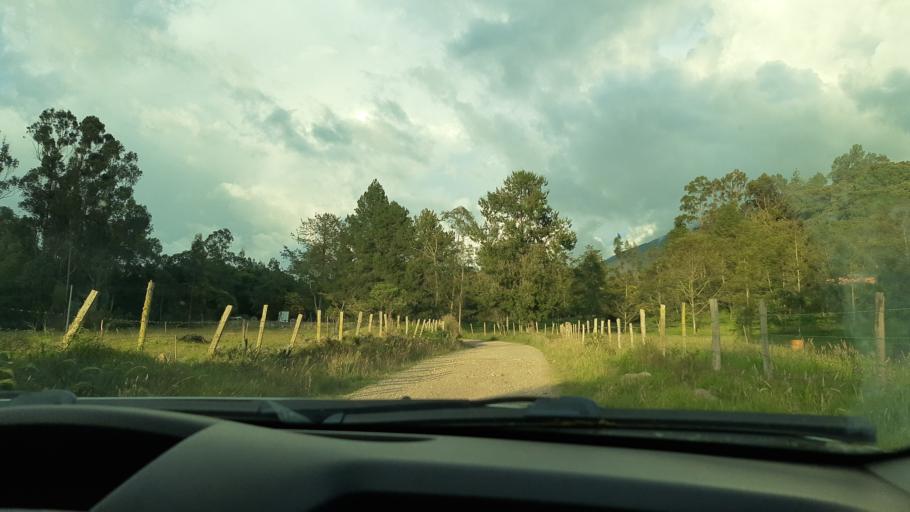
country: CO
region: Boyaca
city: La Capilla
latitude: 5.7164
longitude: -73.4744
